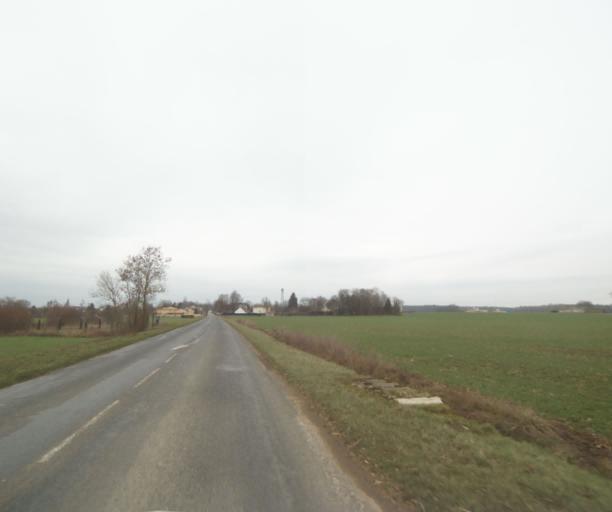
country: FR
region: Champagne-Ardenne
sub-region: Departement de la Haute-Marne
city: Villiers-en-Lieu
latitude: 48.6604
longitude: 4.9083
